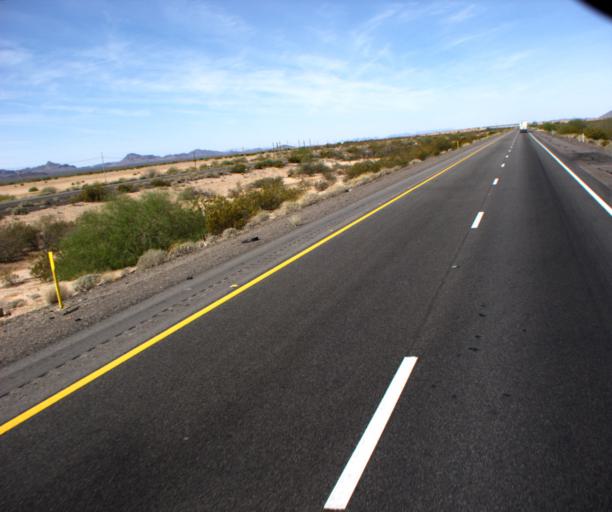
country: US
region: Arizona
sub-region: La Paz County
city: Salome
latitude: 33.5670
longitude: -113.3379
